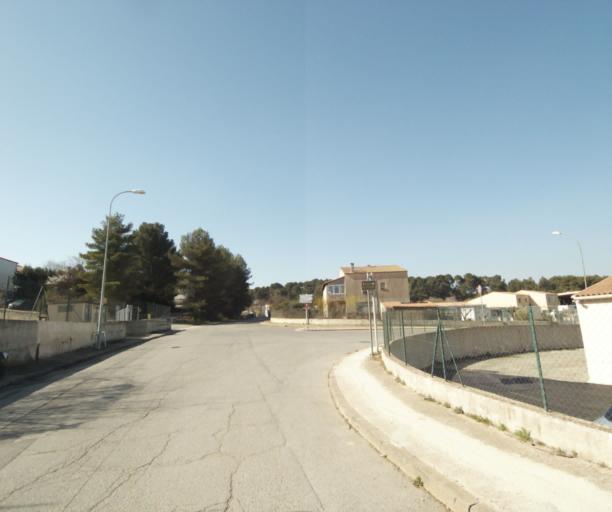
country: FR
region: Provence-Alpes-Cote d'Azur
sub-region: Departement des Bouches-du-Rhone
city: Gardanne
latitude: 43.4452
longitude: 5.4543
